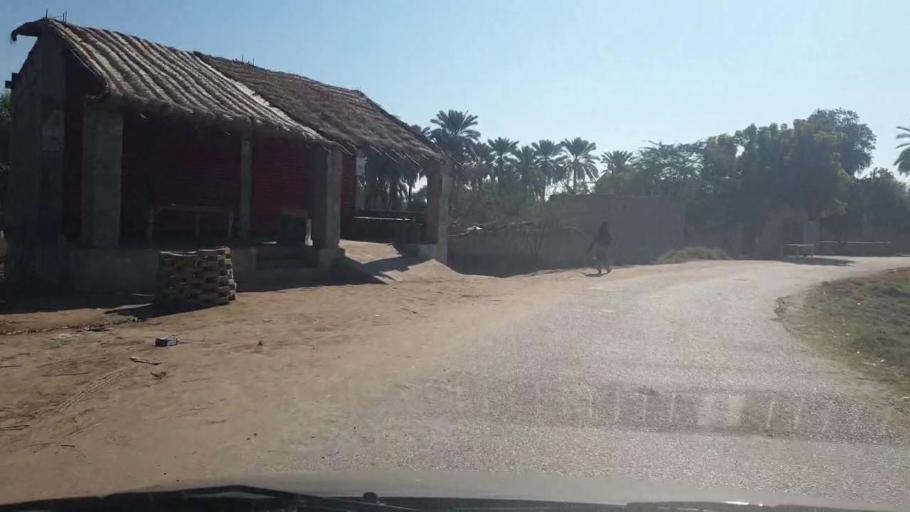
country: PK
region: Sindh
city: Bozdar
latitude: 27.1172
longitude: 68.6350
